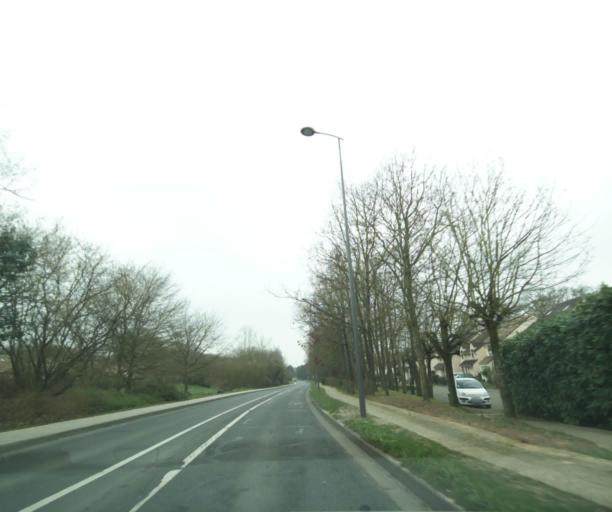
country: FR
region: Ile-de-France
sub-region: Departement du Val-d'Oise
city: Courdimanche
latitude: 49.0434
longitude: 2.0109
